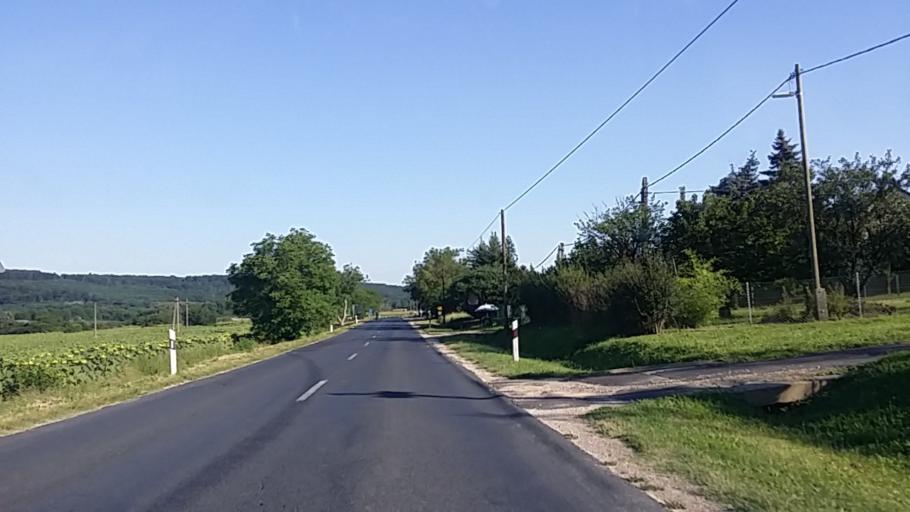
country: HU
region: Zala
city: Cserszegtomaj
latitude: 46.8083
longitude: 17.2057
